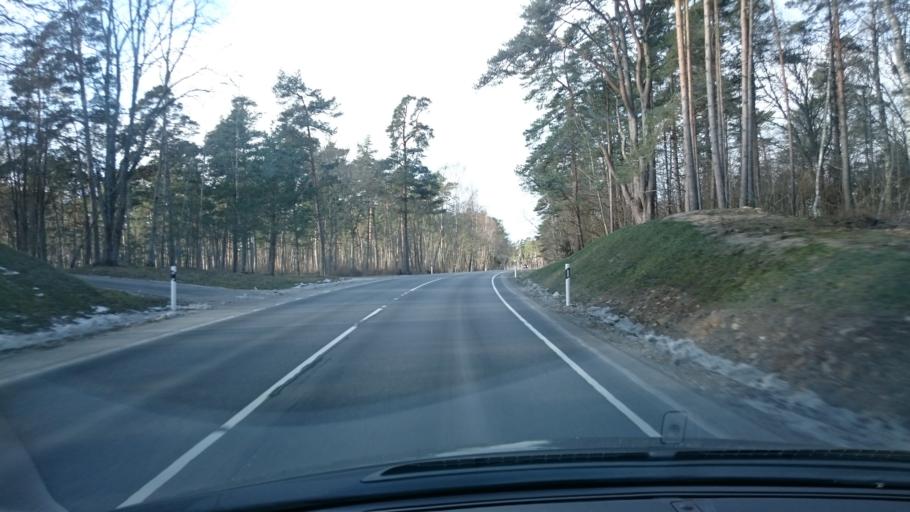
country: EE
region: Harju
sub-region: Keila linn
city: Keila
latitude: 59.3976
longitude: 24.2627
